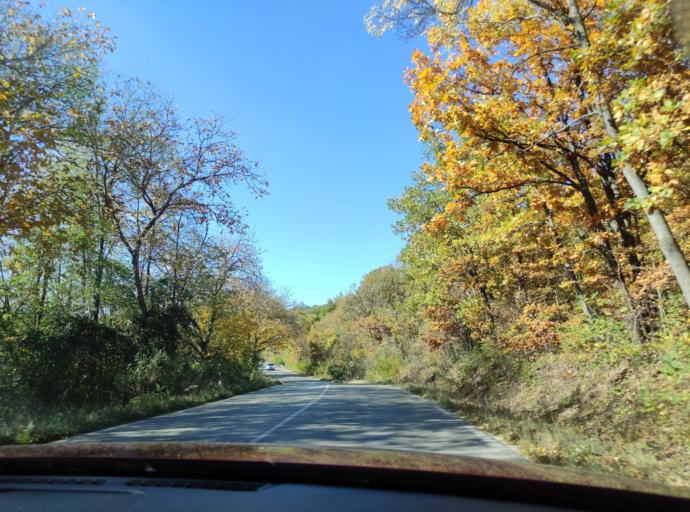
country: BG
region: Montana
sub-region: Obshtina Montana
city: Montana
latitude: 43.4067
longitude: 23.0648
